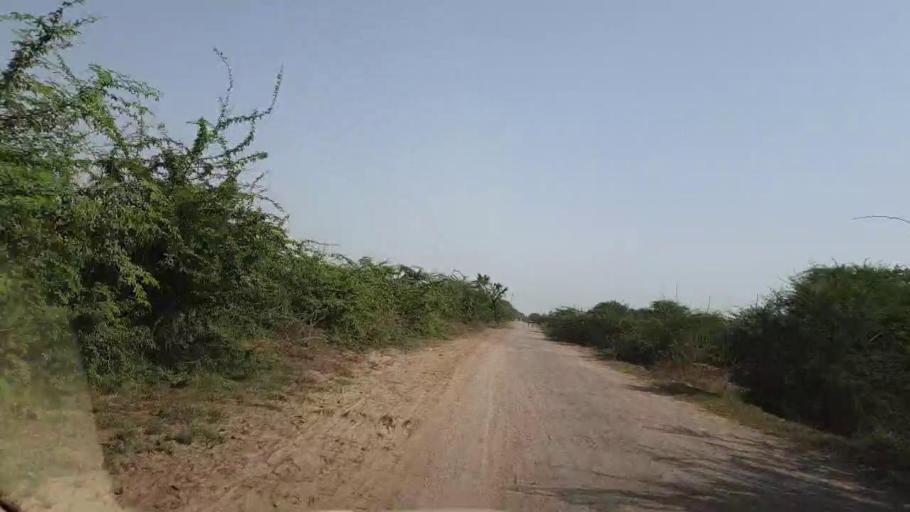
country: PK
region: Sindh
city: Rajo Khanani
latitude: 25.0480
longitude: 68.8363
